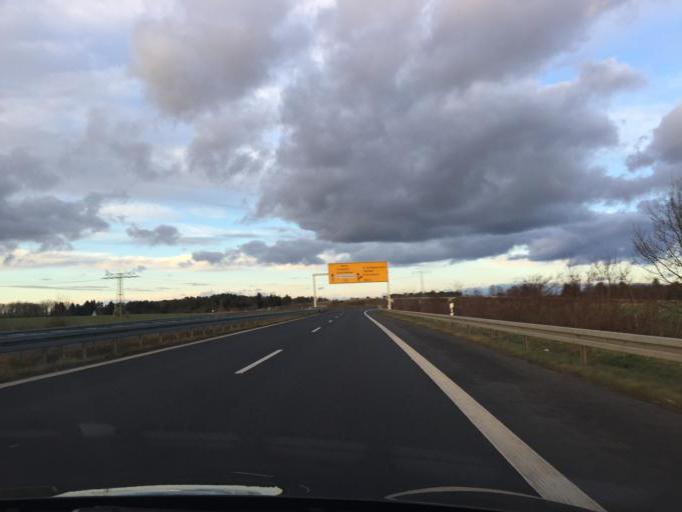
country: DE
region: Brandenburg
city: Rangsdorf
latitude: 52.3379
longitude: 13.4450
